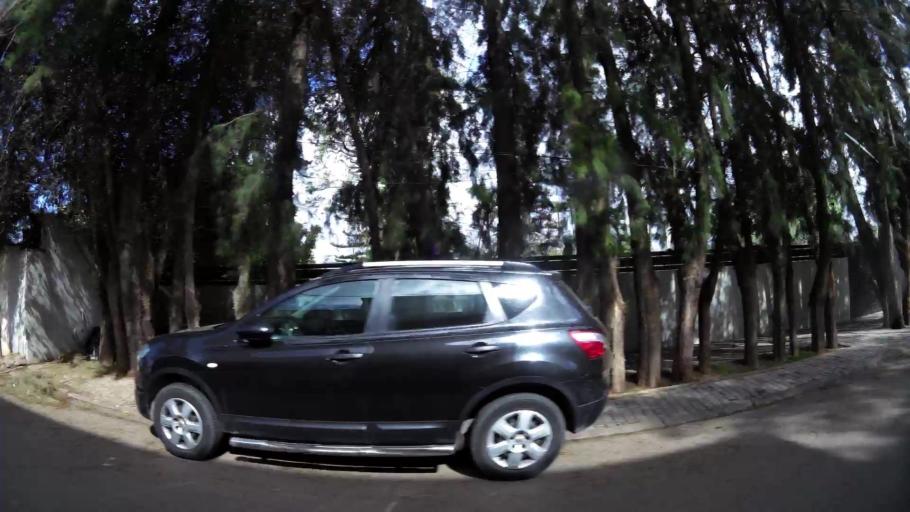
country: MA
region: Grand Casablanca
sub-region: Casablanca
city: Casablanca
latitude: 33.5452
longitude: -7.6252
